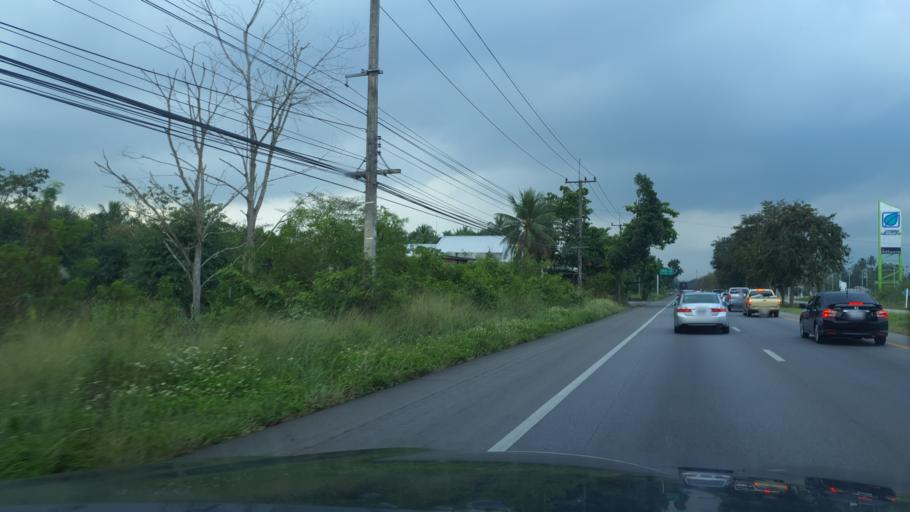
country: TH
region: Prachuap Khiri Khan
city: Bang Saphan
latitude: 11.2168
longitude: 99.4098
